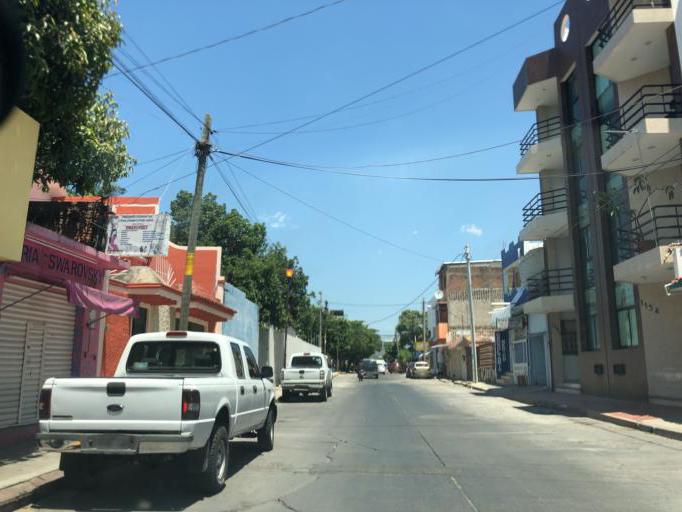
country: MX
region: Chiapas
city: Tuxtla Gutierrez
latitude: 16.7569
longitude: -93.1245
